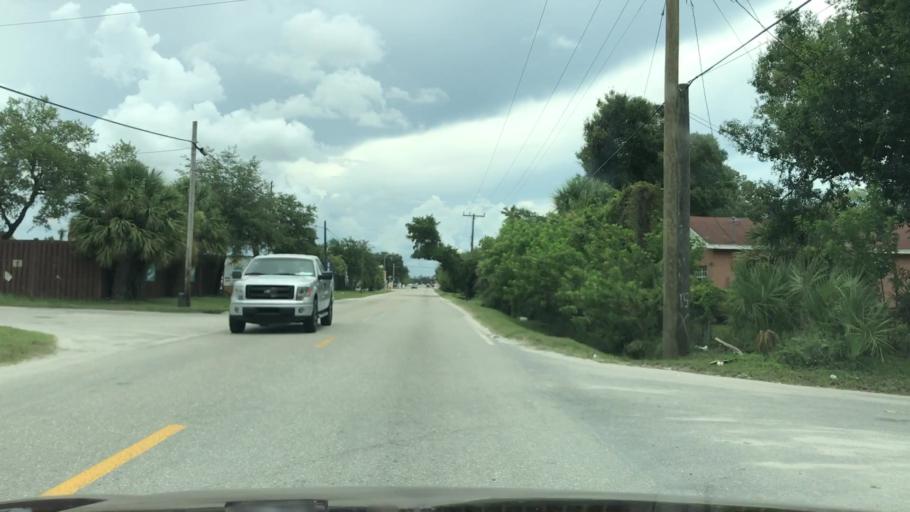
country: US
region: Florida
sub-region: Sarasota County
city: North Sarasota
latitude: 27.3671
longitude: -82.5373
